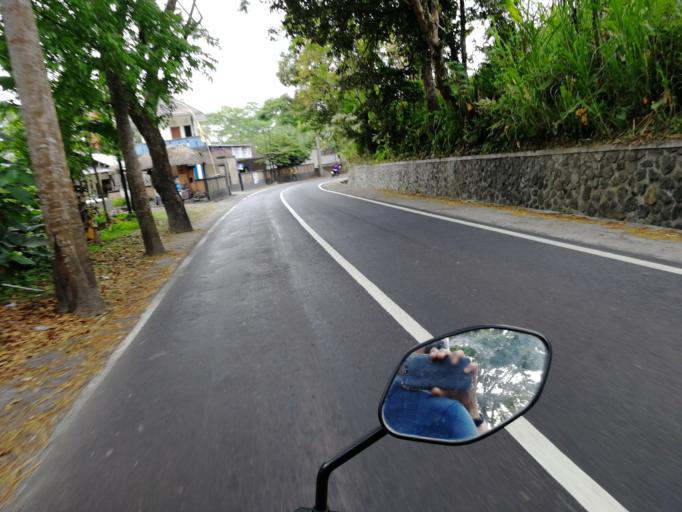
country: ID
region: Bali
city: Banjar Geriana Kangin
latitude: -8.4265
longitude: 115.4412
